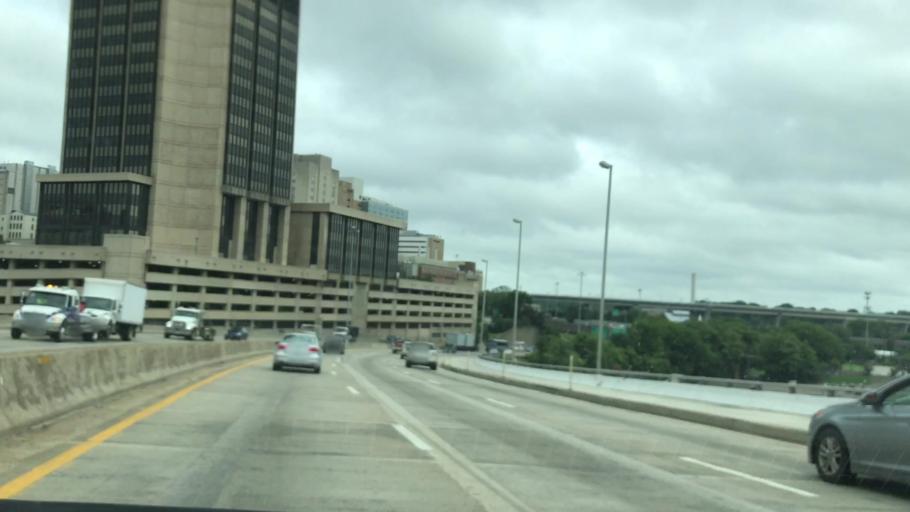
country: US
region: Virginia
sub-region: City of Richmond
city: Richmond
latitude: 37.5346
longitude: -77.4299
